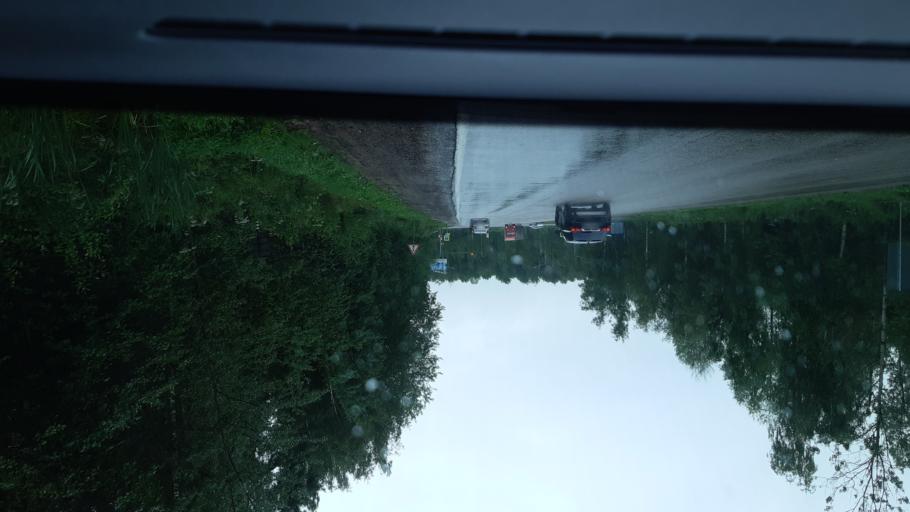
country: RU
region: Smolensk
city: Gagarin
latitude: 55.5016
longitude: 35.0363
